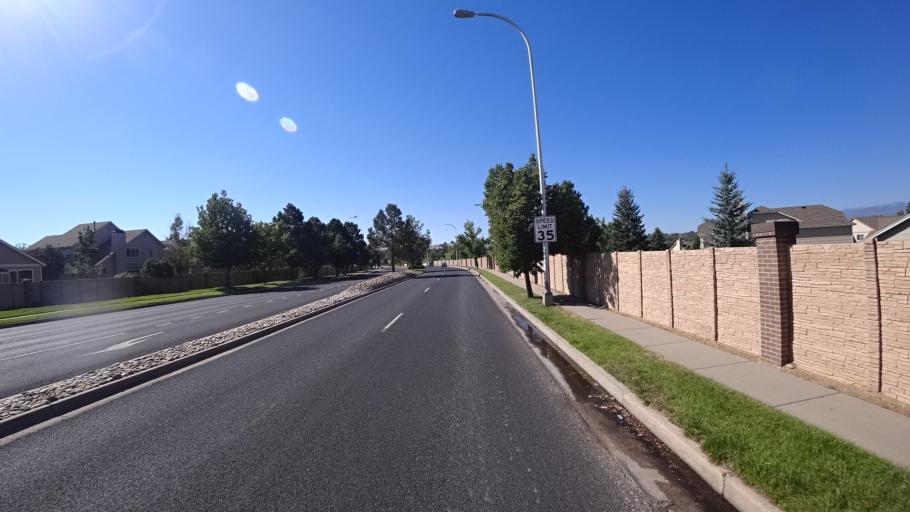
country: US
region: Colorado
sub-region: El Paso County
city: Cimarron Hills
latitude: 38.9321
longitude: -104.7539
